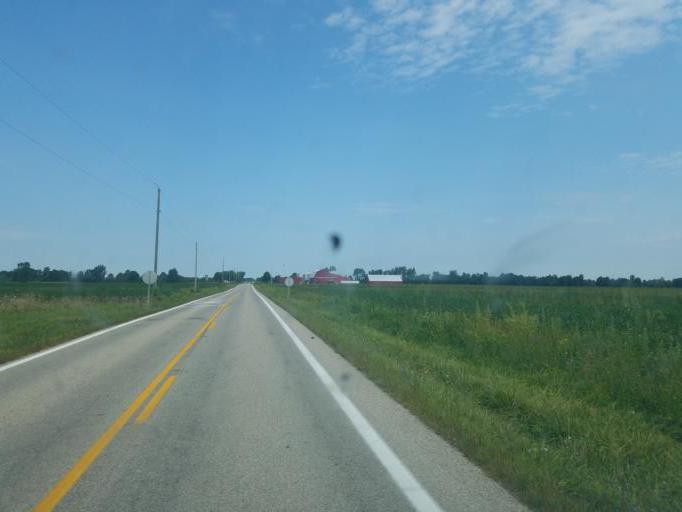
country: US
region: Ohio
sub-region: Marion County
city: Marion
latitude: 40.5880
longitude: -83.2174
